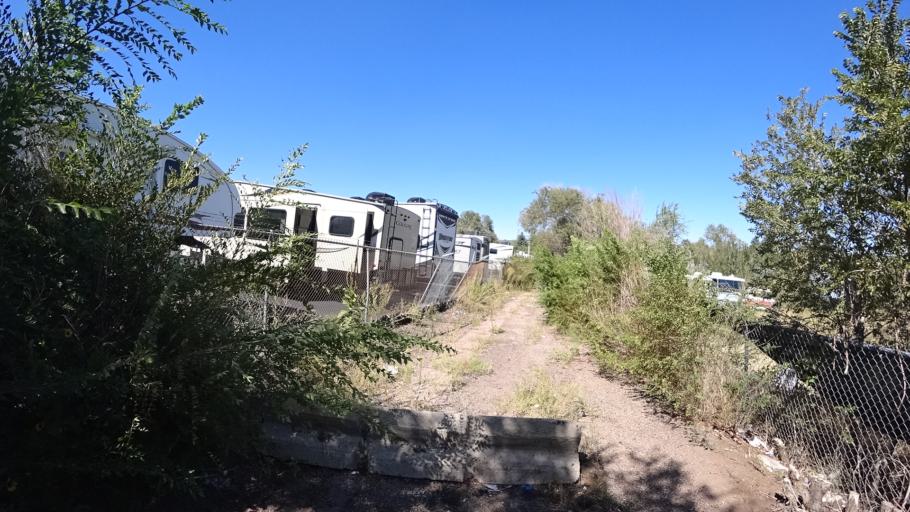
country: US
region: Colorado
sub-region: El Paso County
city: Colorado Springs
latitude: 38.8408
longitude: -104.7692
